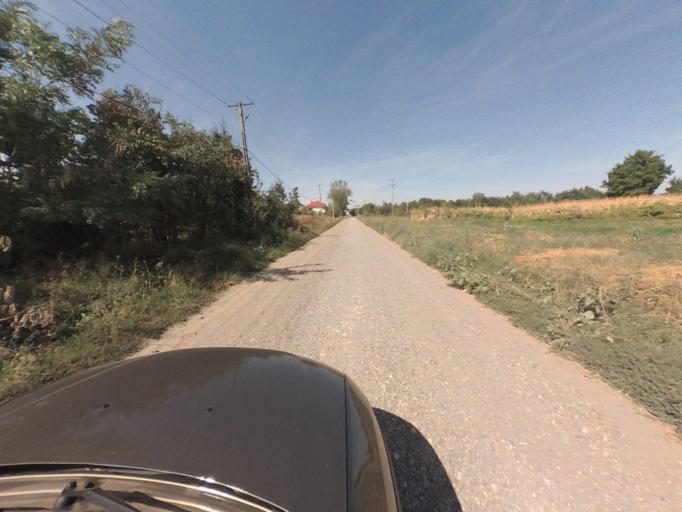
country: RO
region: Vaslui
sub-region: Comuna Deleni
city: Deleni
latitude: 46.5391
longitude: 27.7495
